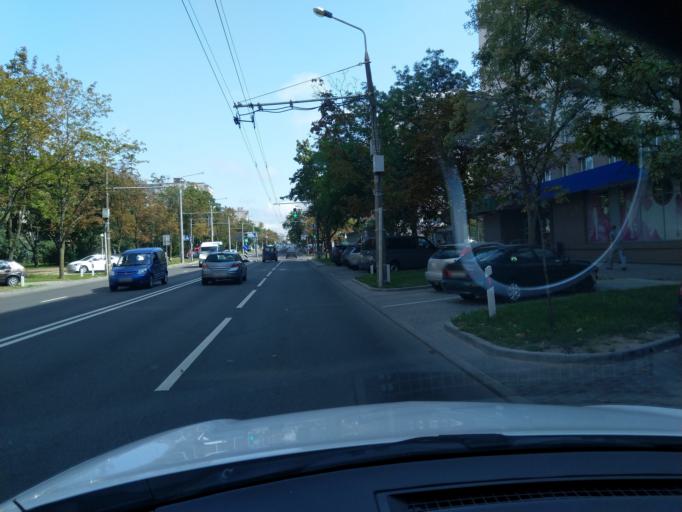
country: BY
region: Minsk
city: Minsk
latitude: 53.9236
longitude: 27.5801
